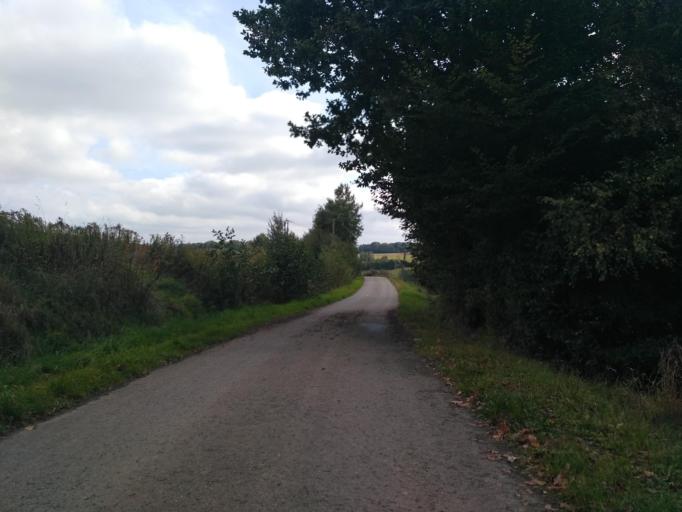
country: PL
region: Subcarpathian Voivodeship
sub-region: Powiat ropczycko-sedziszowski
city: Niedzwiada
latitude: 49.9420
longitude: 21.5153
